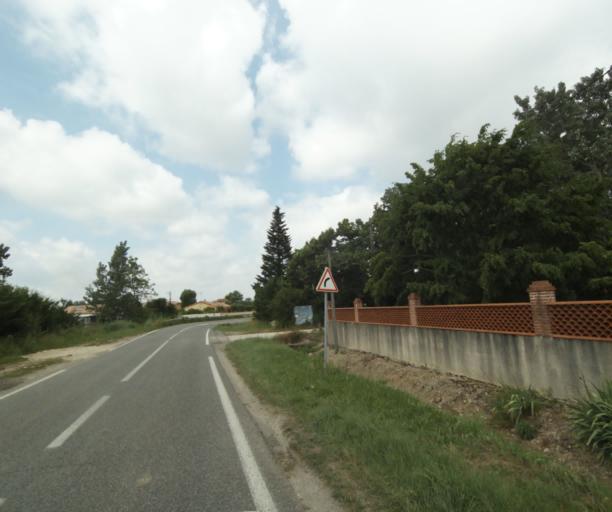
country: FR
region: Midi-Pyrenees
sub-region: Departement du Tarn-et-Garonne
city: Montauban
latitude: 44.0508
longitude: 1.3856
